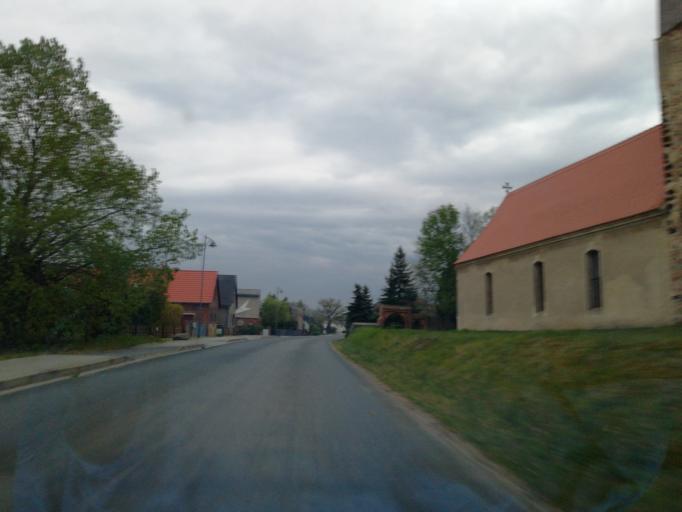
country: DE
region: Brandenburg
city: Calau
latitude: 51.7737
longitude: 13.8727
